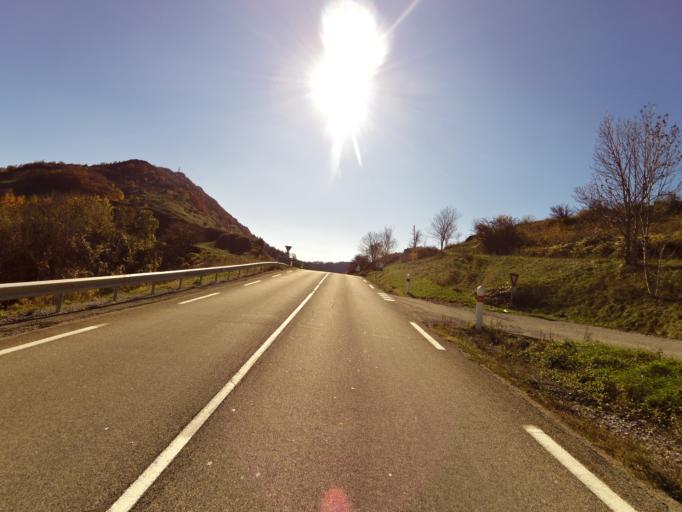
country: FR
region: Rhone-Alpes
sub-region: Departement de l'Ardeche
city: Saint-Priest
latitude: 44.7189
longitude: 4.4930
